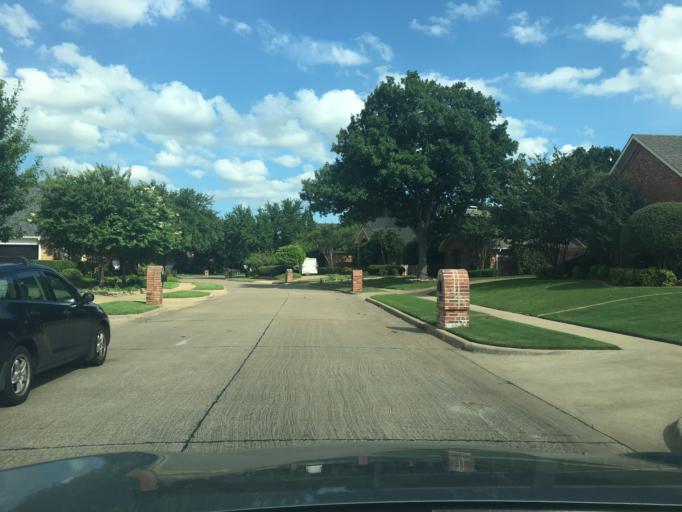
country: US
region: Texas
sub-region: Dallas County
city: Garland
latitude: 32.9367
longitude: -96.6734
